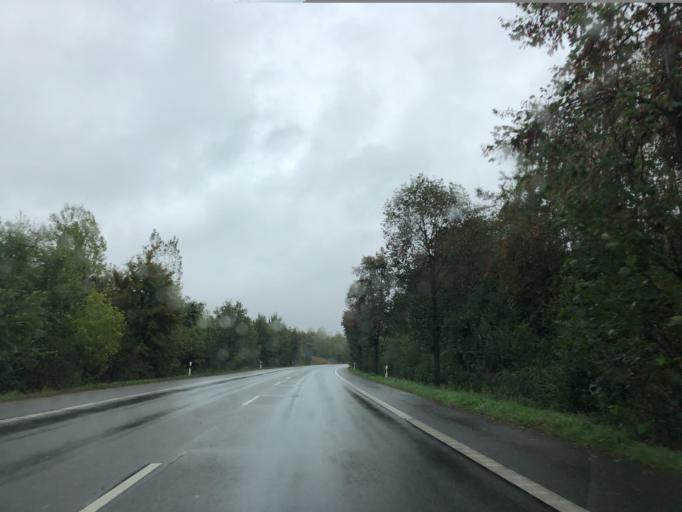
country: DE
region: North Rhine-Westphalia
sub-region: Regierungsbezirk Koln
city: Bedburg
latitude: 51.0279
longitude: 6.5781
